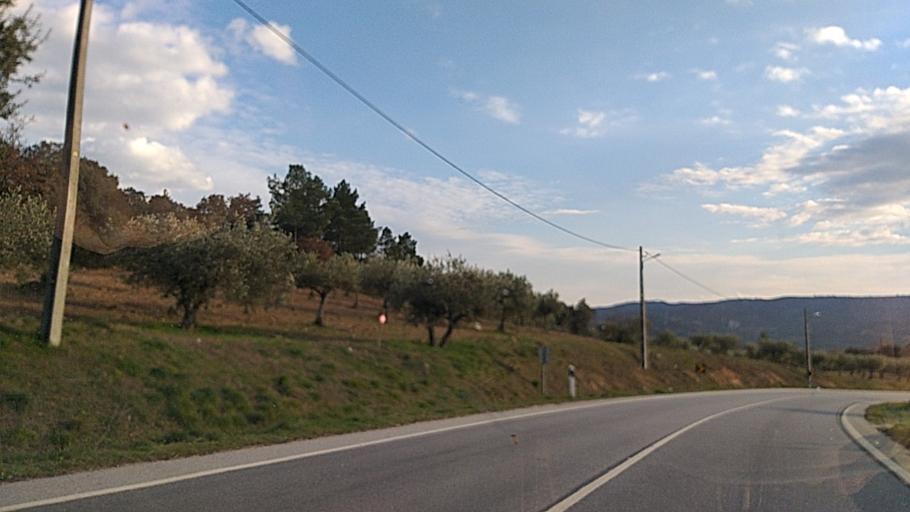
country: ES
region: Castille and Leon
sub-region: Provincia de Salamanca
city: Aldea del Obispo
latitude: 40.7031
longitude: -6.9264
